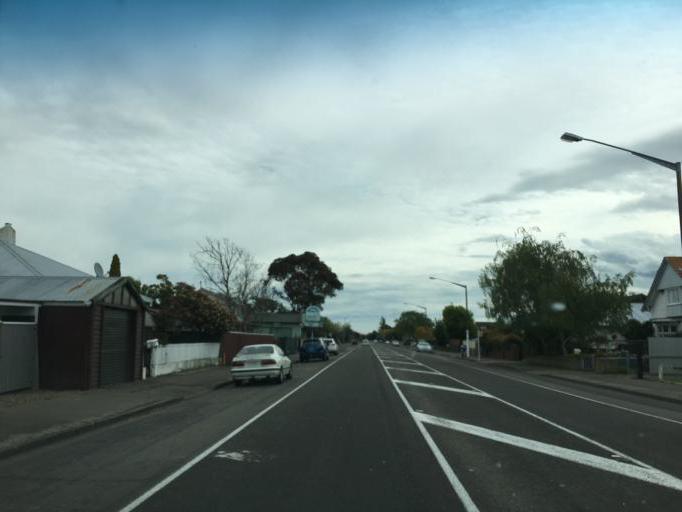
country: NZ
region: Manawatu-Wanganui
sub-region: Palmerston North City
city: Palmerston North
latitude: -40.3541
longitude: 175.5968
